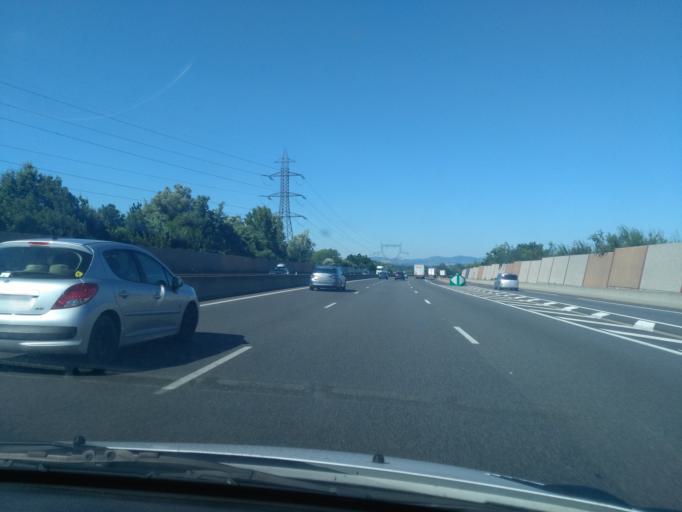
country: FR
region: Rhone-Alpes
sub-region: Departement de l'Ain
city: Massieux
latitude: 45.9044
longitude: 4.8287
